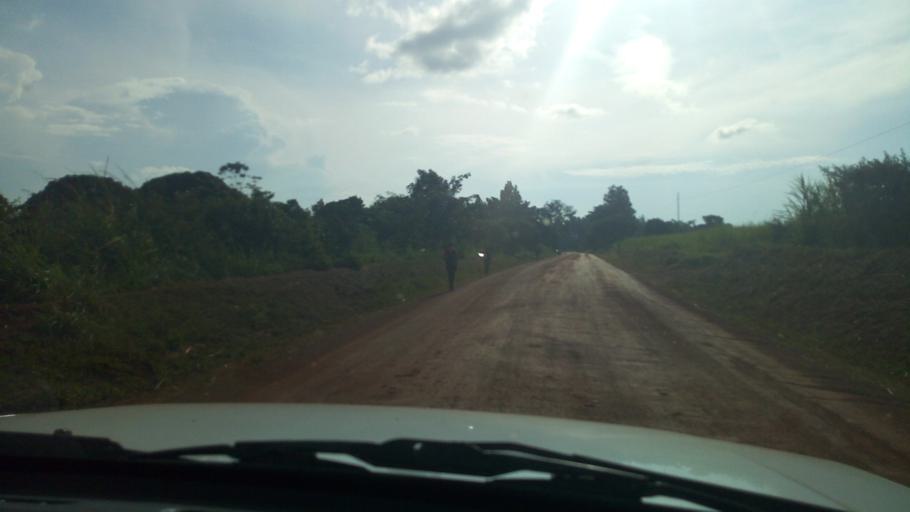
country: UG
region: Western Region
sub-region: Masindi District
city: Masindi
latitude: 1.6754
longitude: 31.6666
